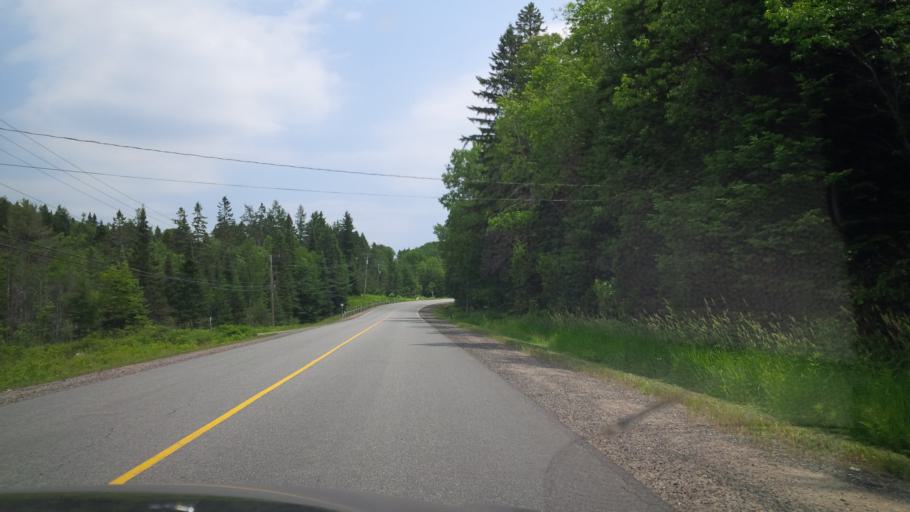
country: CA
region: Ontario
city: Huntsville
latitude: 45.5318
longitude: -79.3071
